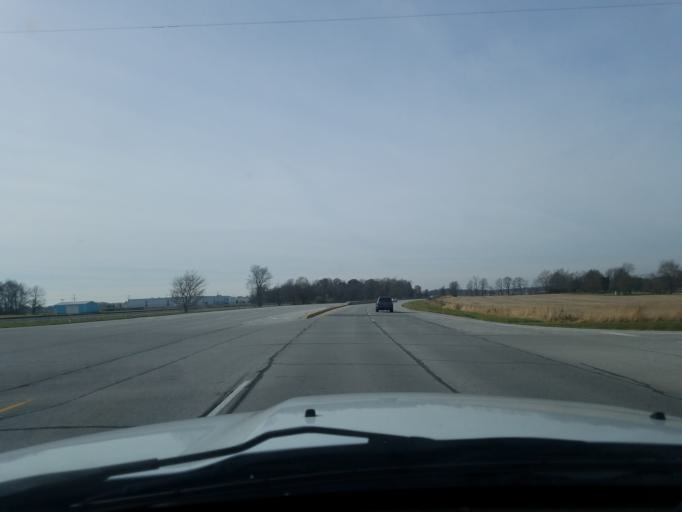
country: US
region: Indiana
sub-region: Delaware County
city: Yorktown
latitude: 40.2165
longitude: -85.5414
